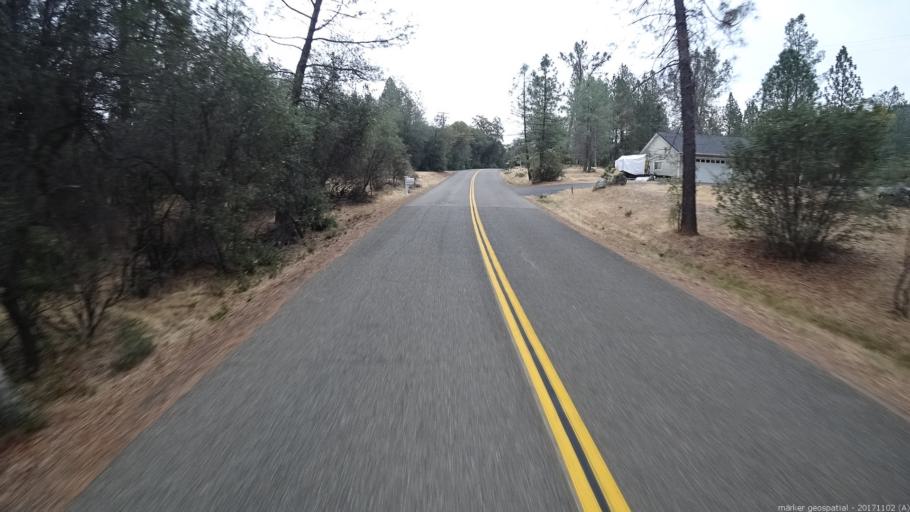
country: US
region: California
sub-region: Shasta County
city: Central Valley (historical)
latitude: 40.6646
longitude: -122.4031
